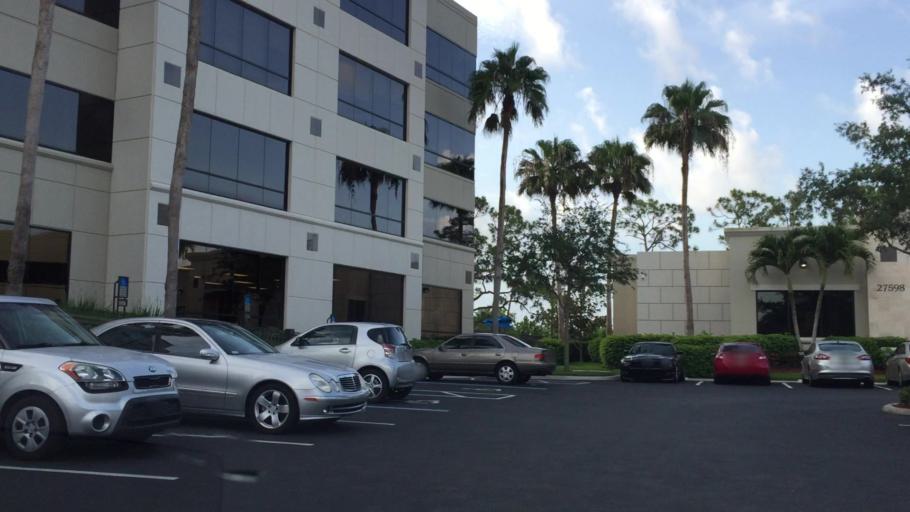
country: US
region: Florida
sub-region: Lee County
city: Bonita Springs
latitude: 26.3402
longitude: -81.8084
